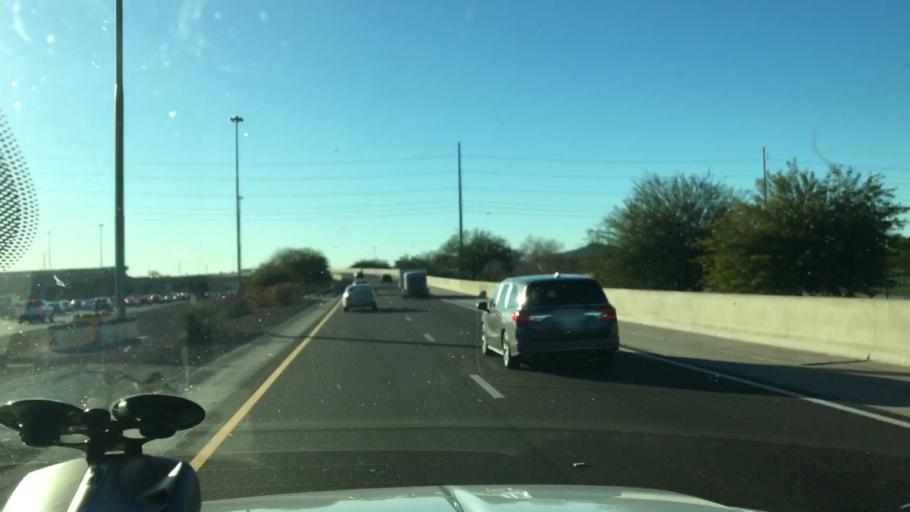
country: US
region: Arizona
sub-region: Maricopa County
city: Paradise Valley
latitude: 33.6736
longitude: -111.9938
